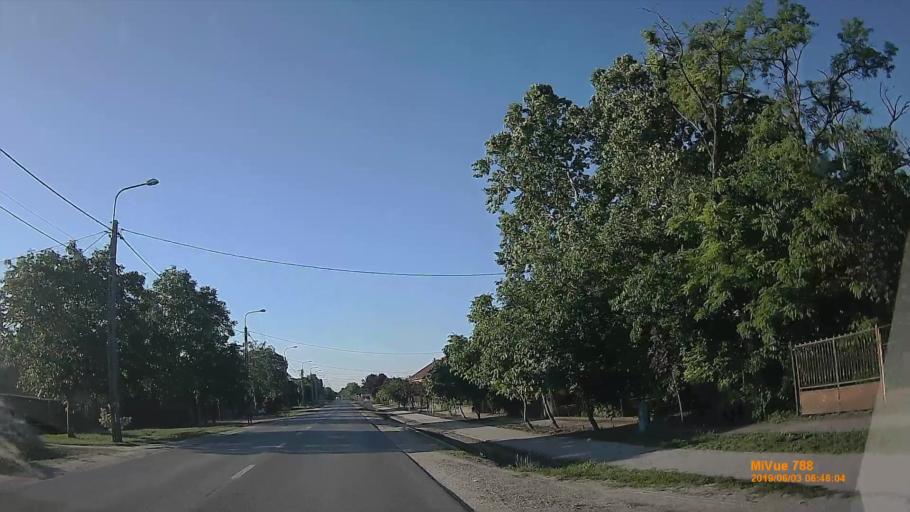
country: HU
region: Pest
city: Bugyi
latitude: 47.2336
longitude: 19.1411
